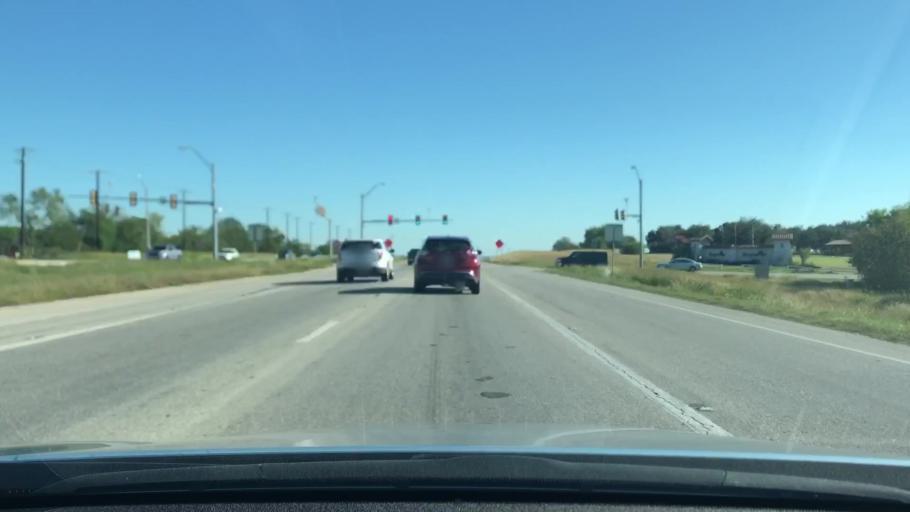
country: US
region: Texas
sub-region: Bexar County
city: Converse
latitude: 29.5155
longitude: -98.2895
